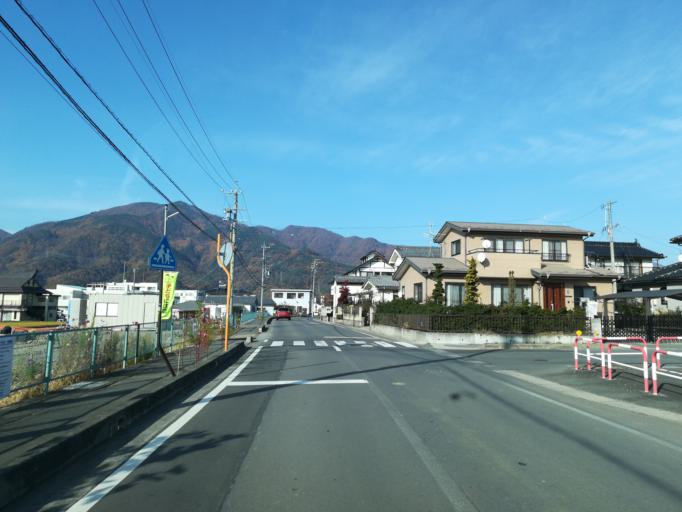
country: JP
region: Nagano
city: Ueda
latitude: 36.4035
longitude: 138.2802
